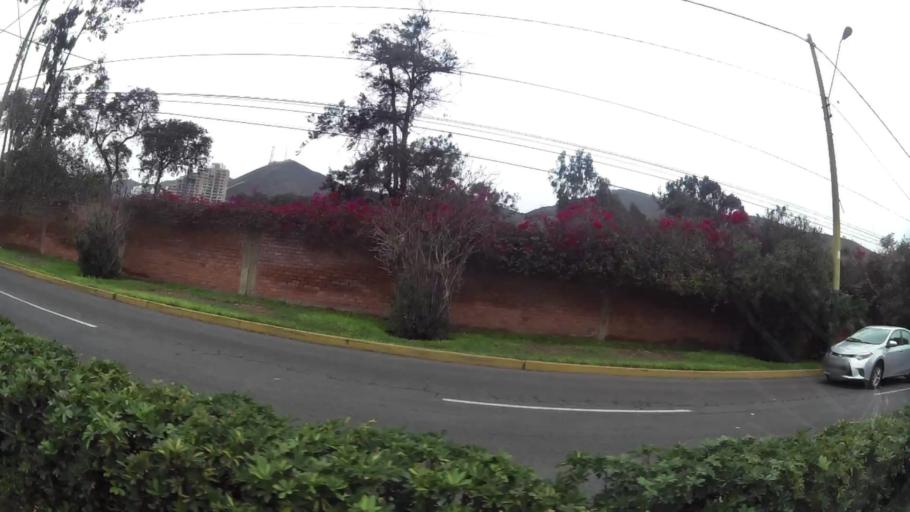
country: PE
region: Lima
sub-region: Lima
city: La Molina
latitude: -12.0895
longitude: -76.9670
